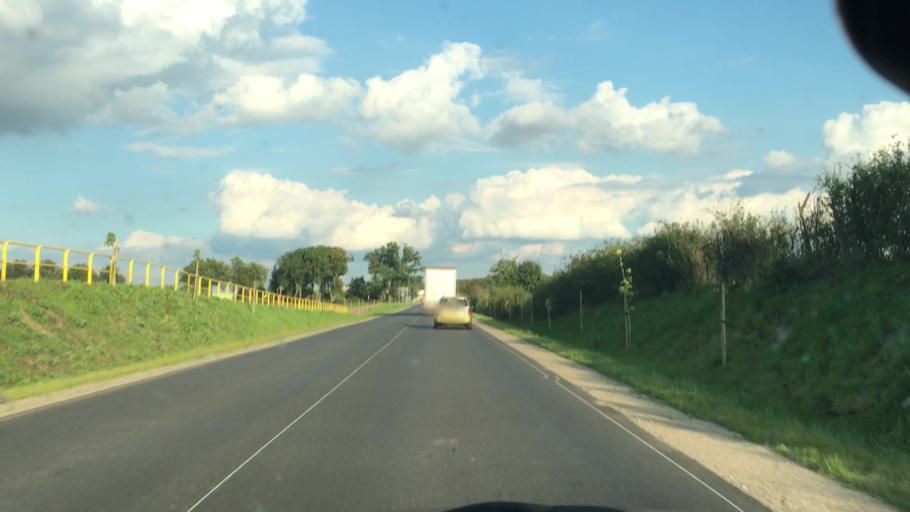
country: PL
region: Pomeranian Voivodeship
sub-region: Powiat tczewski
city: Pelplin
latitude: 53.9280
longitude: 18.6323
